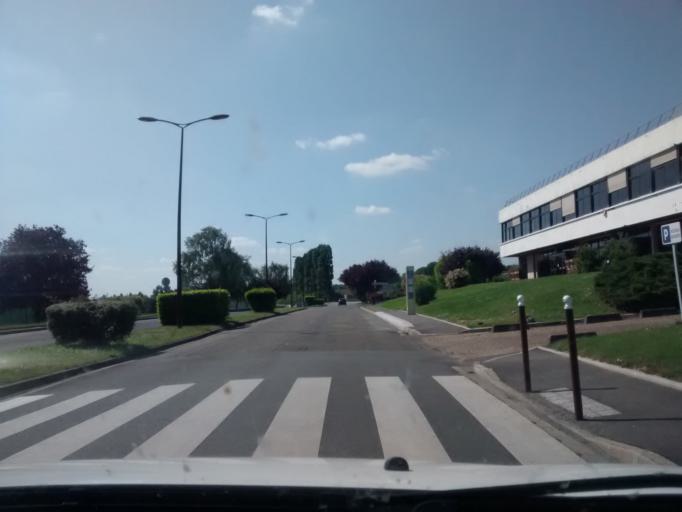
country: FR
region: Ile-de-France
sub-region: Departement des Yvelines
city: Buc
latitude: 48.7855
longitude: 2.1101
